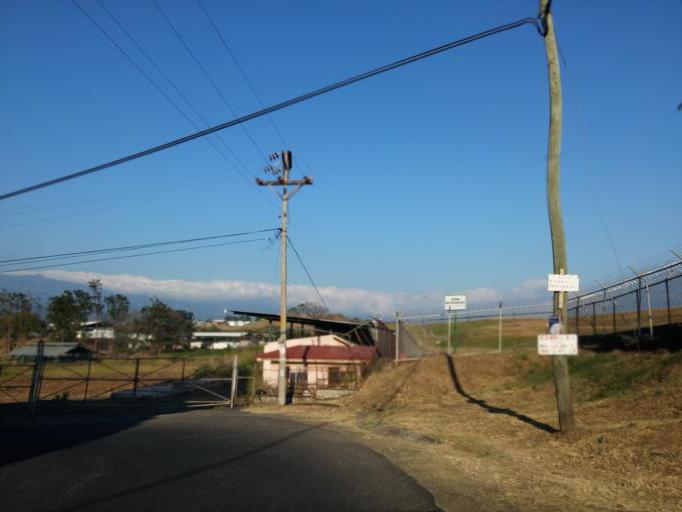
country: CR
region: Alajuela
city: Alajuela
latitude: 9.9917
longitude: -84.2209
